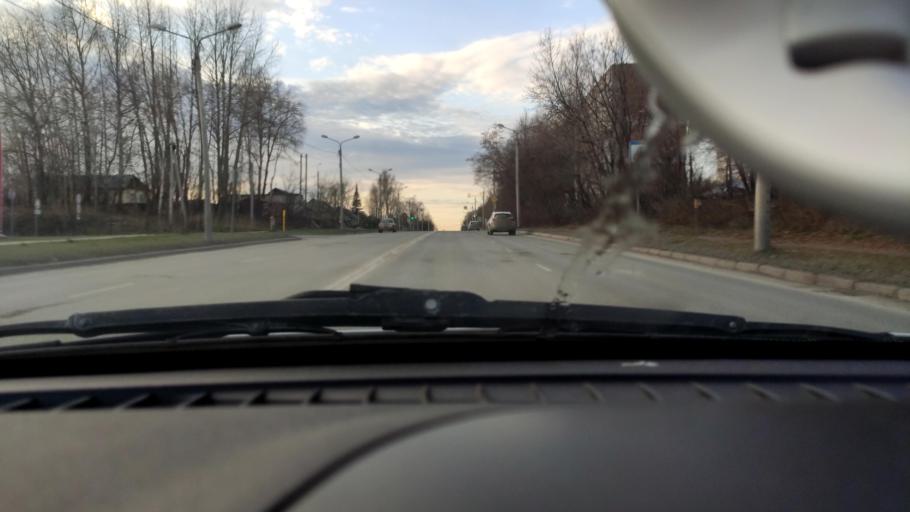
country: RU
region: Perm
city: Perm
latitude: 58.0653
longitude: 56.3648
